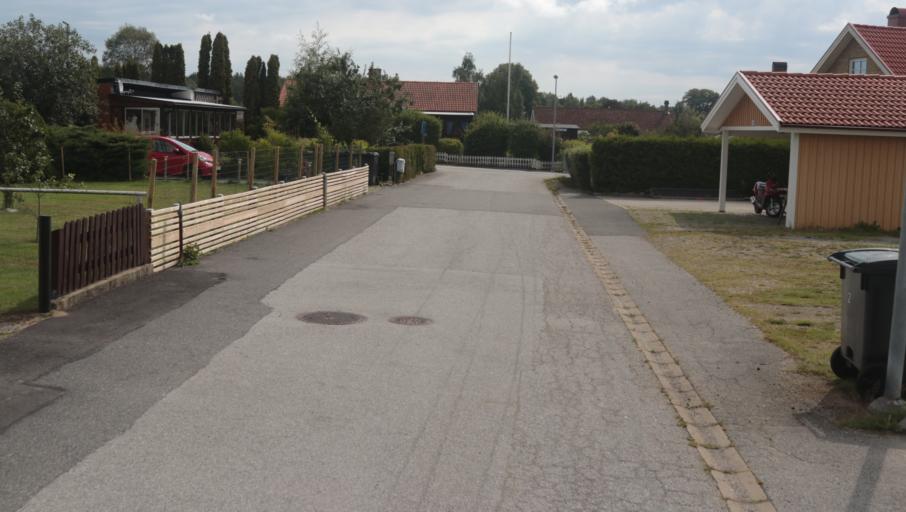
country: SE
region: Blekinge
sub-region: Karlshamns Kommun
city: Morrum
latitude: 56.1977
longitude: 14.7528
